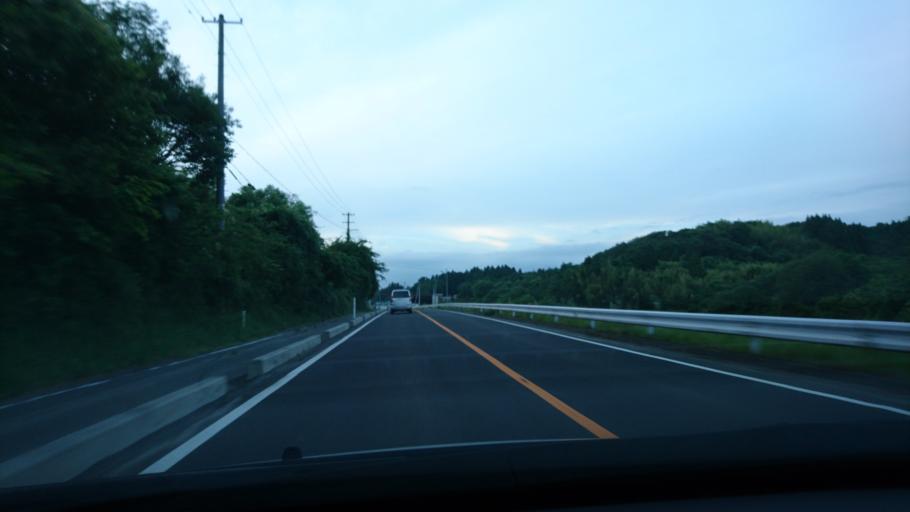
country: JP
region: Miyagi
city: Furukawa
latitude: 38.7619
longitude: 141.0037
